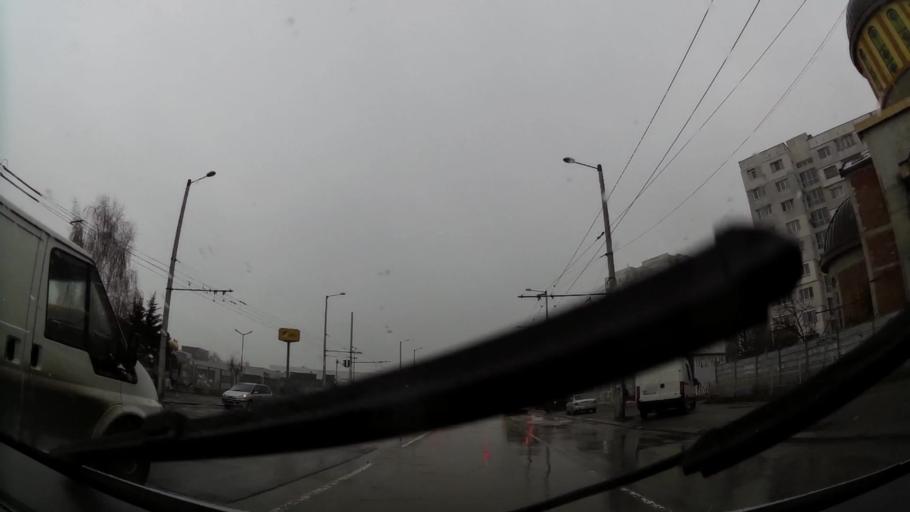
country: BG
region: Sofia-Capital
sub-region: Stolichna Obshtina
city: Sofia
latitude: 42.6549
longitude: 23.4001
